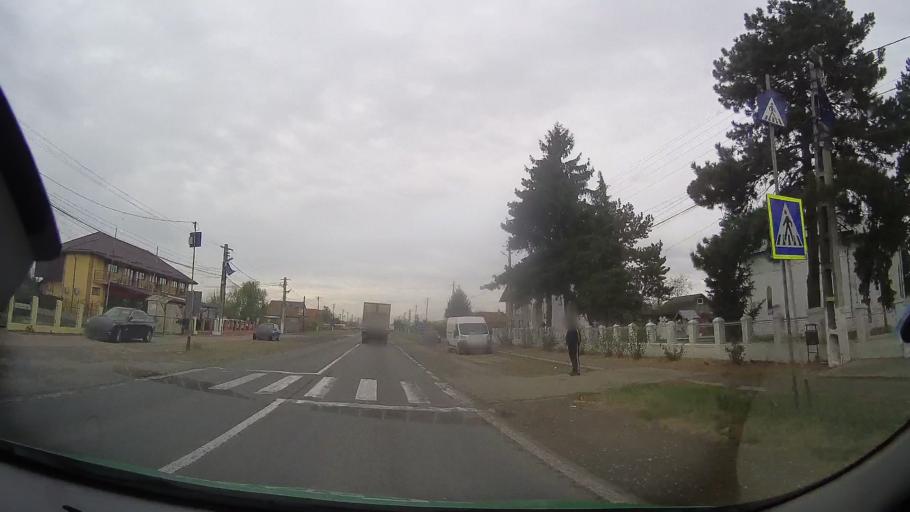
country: RO
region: Prahova
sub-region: Comuna Tomsani
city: Loloiasca
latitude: 44.9679
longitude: 26.2904
